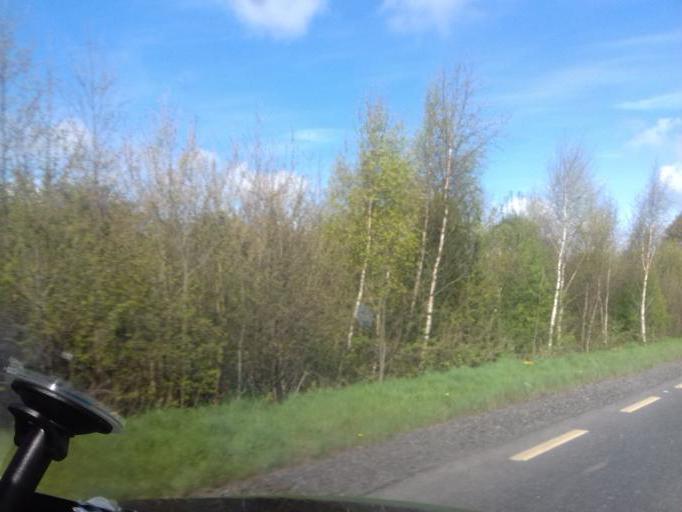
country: IE
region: Ulster
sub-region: An Cabhan
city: Mullagh
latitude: 53.7485
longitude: -6.9790
